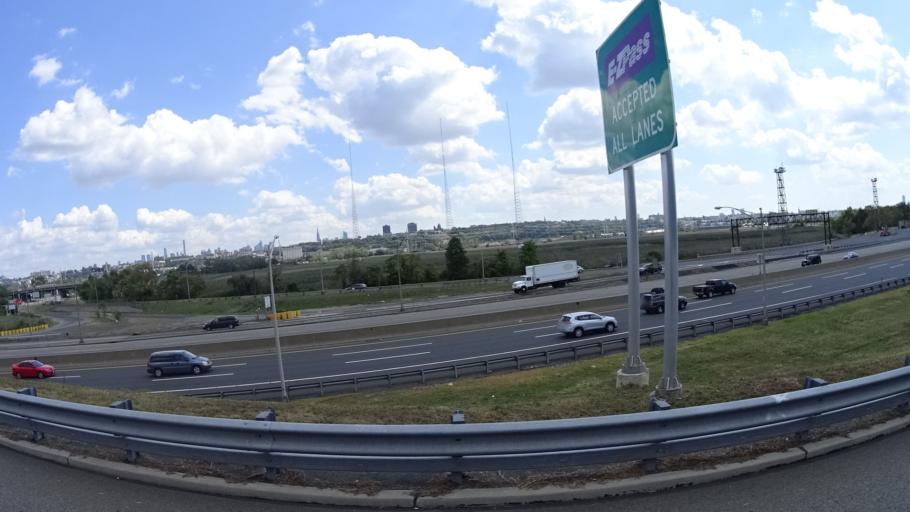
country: US
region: New Jersey
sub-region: Hudson County
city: Secaucus
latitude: 40.7805
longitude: -74.0568
